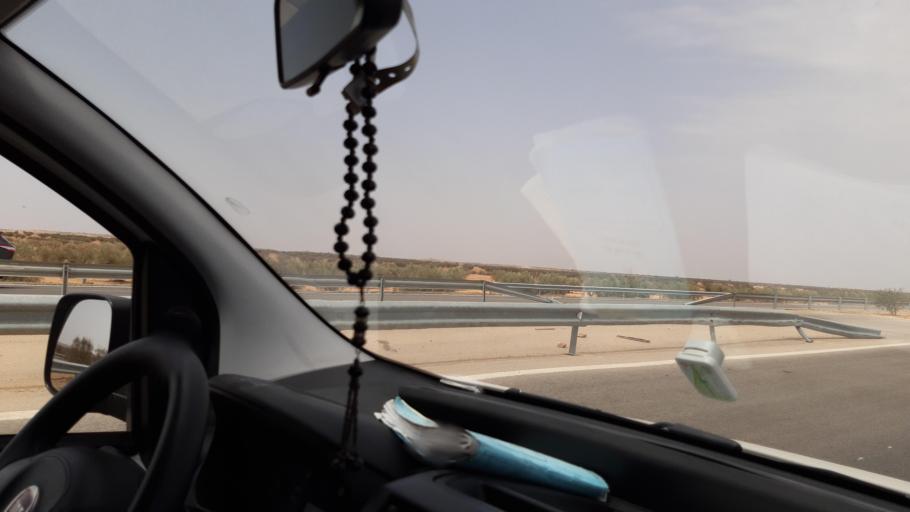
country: TN
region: Safaqis
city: Bi'r `Ali Bin Khalifah
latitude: 34.5902
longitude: 10.4170
